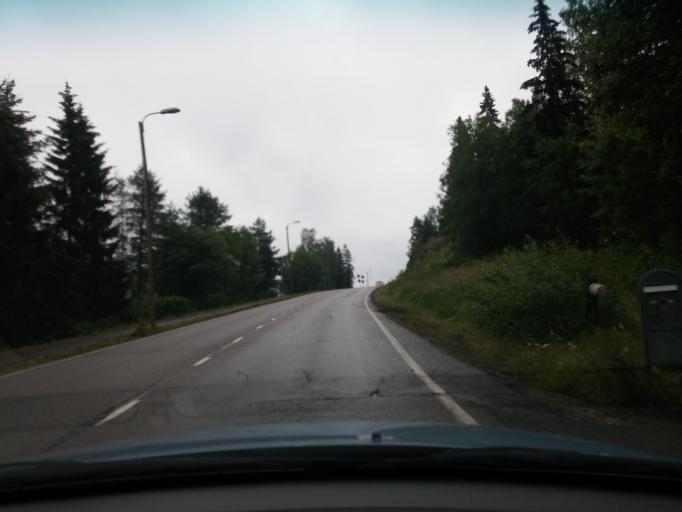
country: FI
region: Uusimaa
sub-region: Helsinki
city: Nurmijaervi
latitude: 60.3628
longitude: 24.7463
